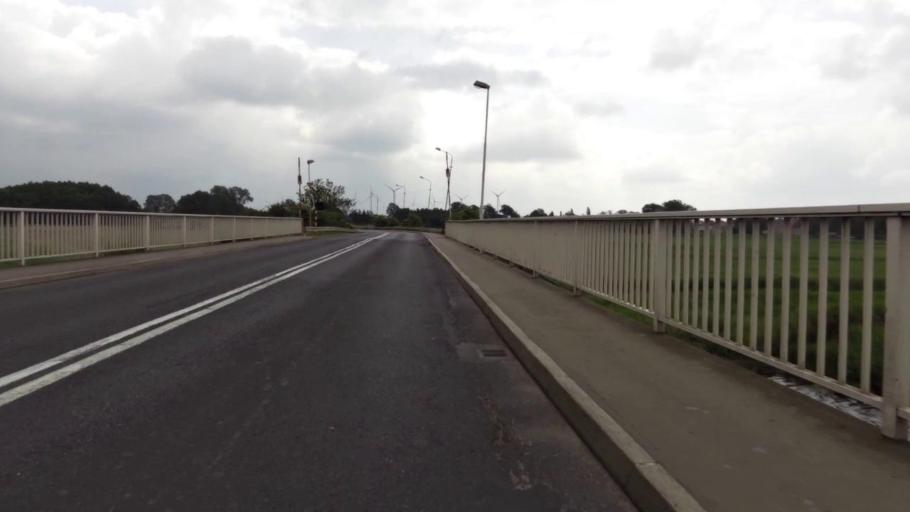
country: PL
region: West Pomeranian Voivodeship
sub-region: Powiat kamienski
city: Wolin
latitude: 53.8434
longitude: 14.6204
